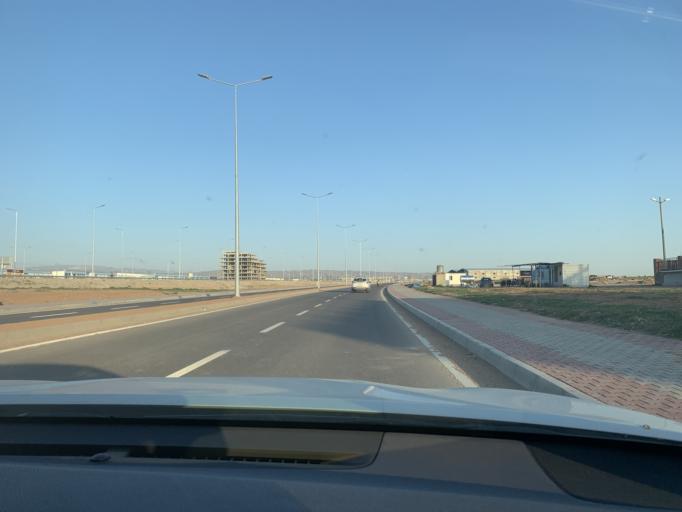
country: IQ
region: Arbil
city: Erbil
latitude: 36.2852
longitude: 44.0475
